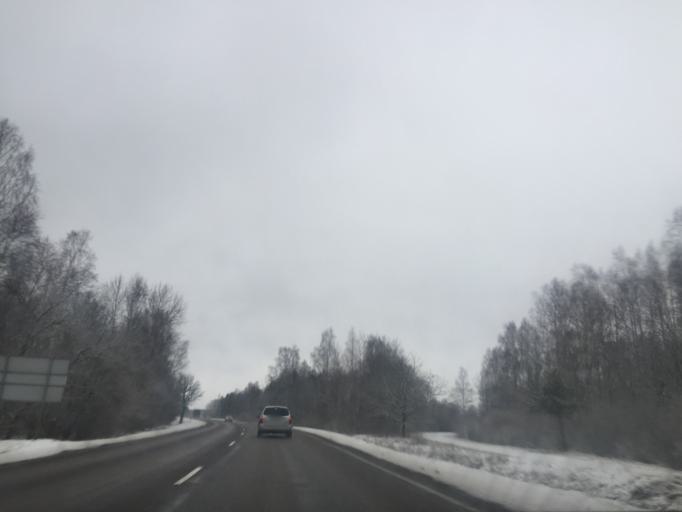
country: EE
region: Laeaene
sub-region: Lihula vald
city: Lihula
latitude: 58.6314
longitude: 23.6863
